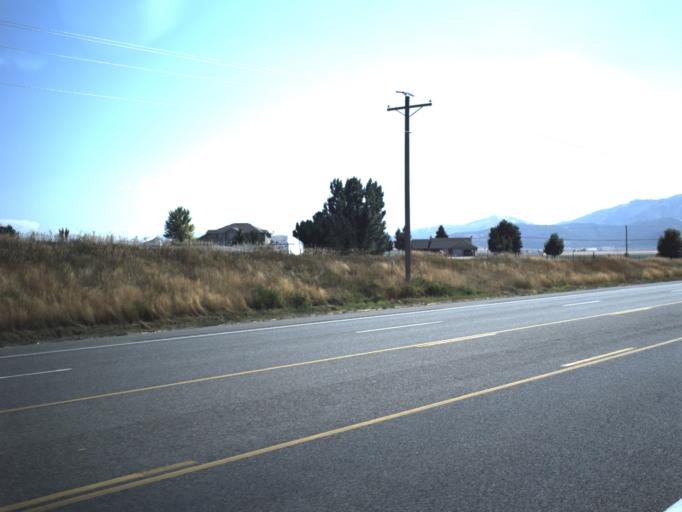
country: US
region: Utah
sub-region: Cache County
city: Wellsville
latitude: 41.6366
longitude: -111.9196
